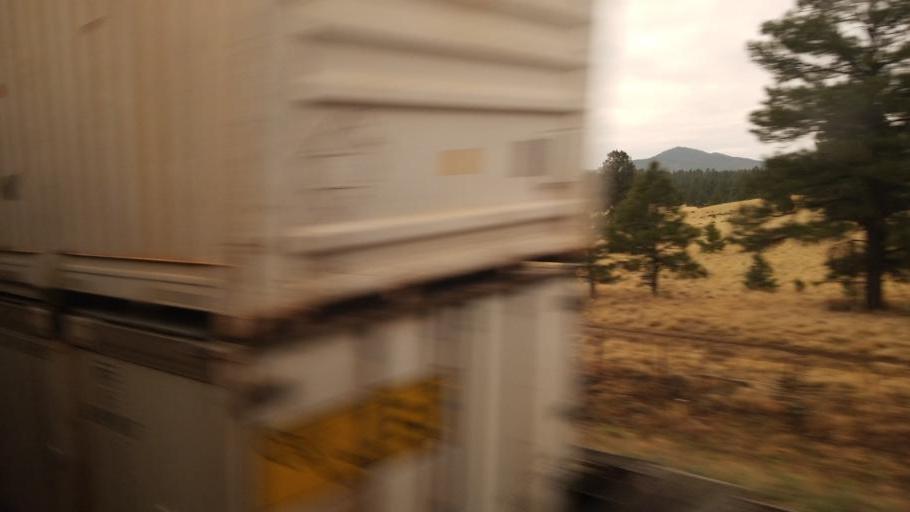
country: US
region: Arizona
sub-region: Coconino County
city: Parks
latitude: 35.2460
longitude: -111.9705
